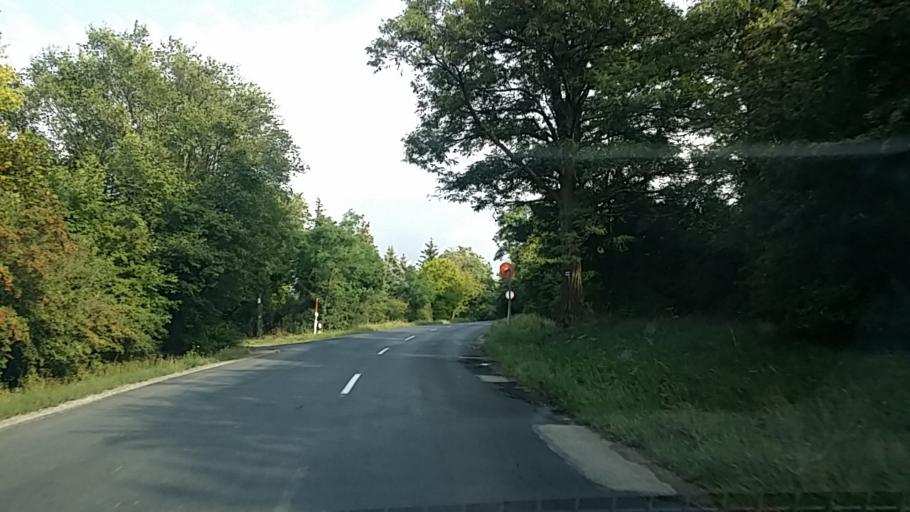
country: HU
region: Gyor-Moson-Sopron
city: Sopron
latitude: 47.6753
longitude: 16.6278
